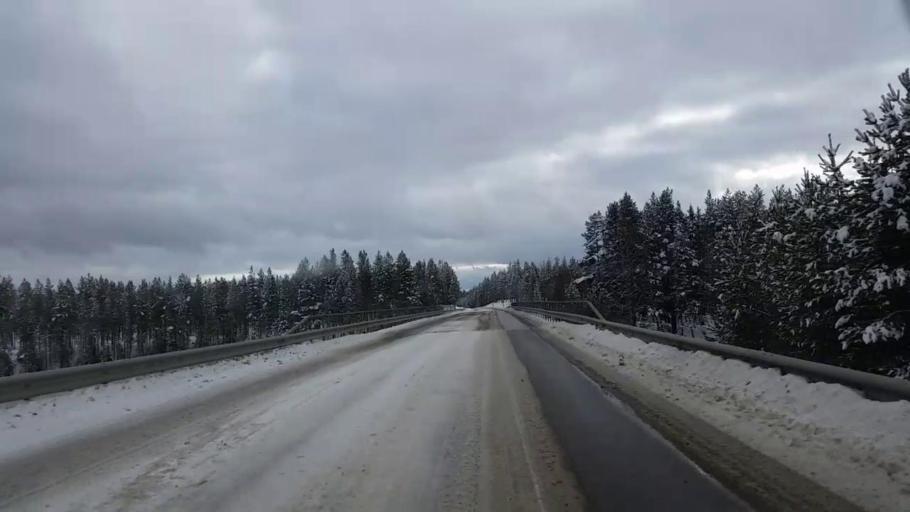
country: SE
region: Jaemtland
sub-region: Harjedalens Kommun
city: Sveg
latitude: 62.1228
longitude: 15.0356
